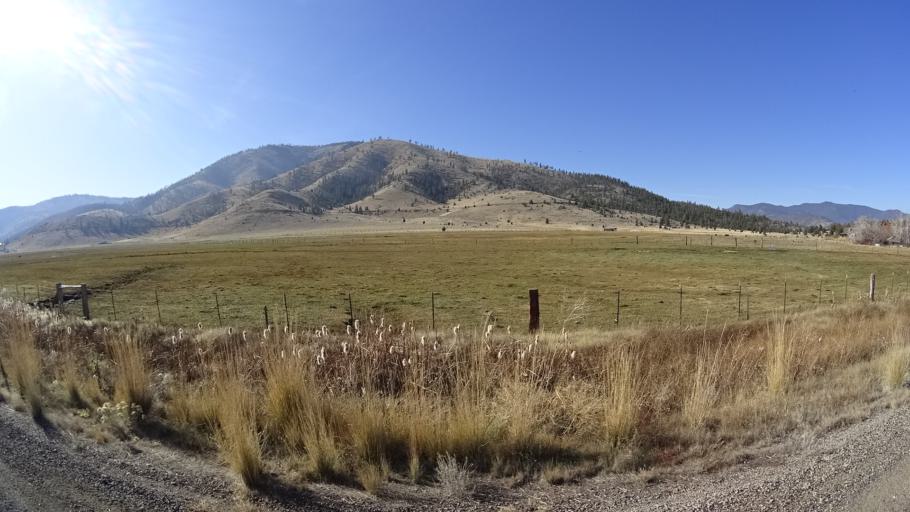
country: US
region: California
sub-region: Siskiyou County
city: Weed
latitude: 41.4897
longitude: -122.5054
